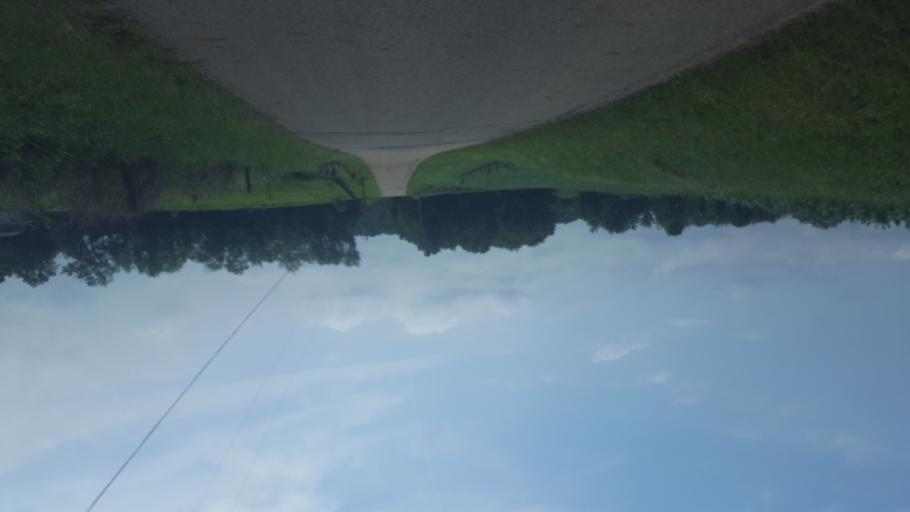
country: US
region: Ohio
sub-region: Licking County
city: Utica
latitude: 40.1865
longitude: -82.4483
